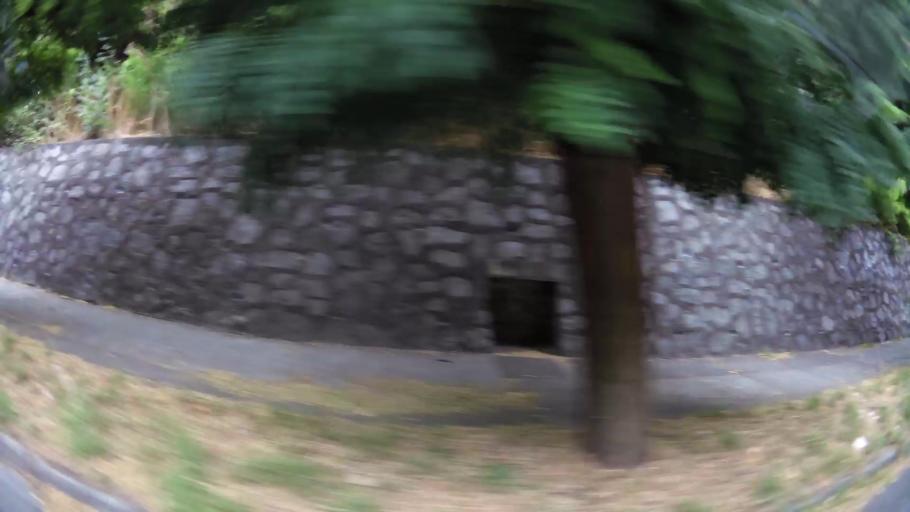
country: CL
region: Biobio
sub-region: Provincia de Concepcion
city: Concepcion
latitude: -36.8249
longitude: -73.0337
